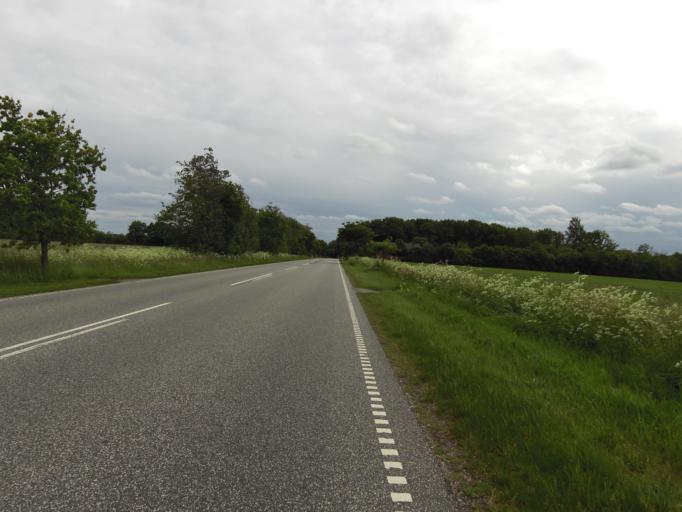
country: DK
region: South Denmark
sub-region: Haderslev Kommune
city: Gram
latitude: 55.3172
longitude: 9.0641
